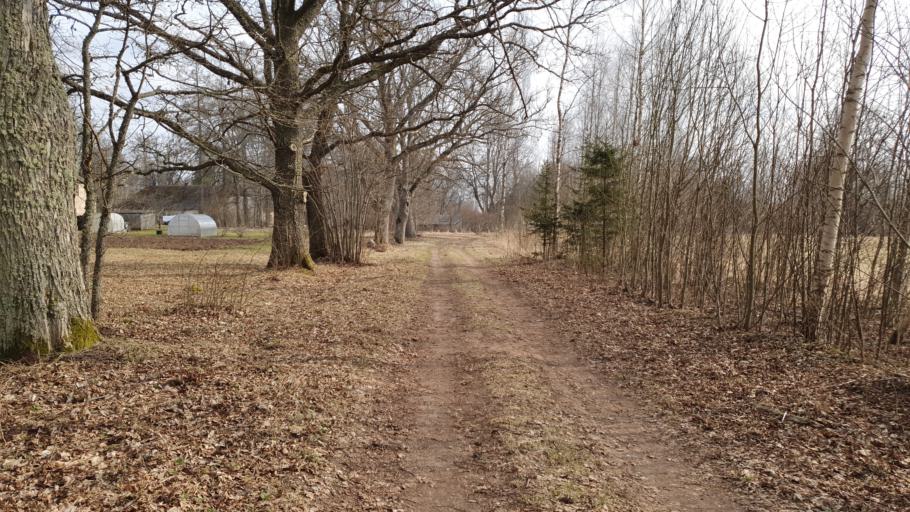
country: LV
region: Beverina
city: Murmuiza
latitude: 57.5490
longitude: 25.5281
